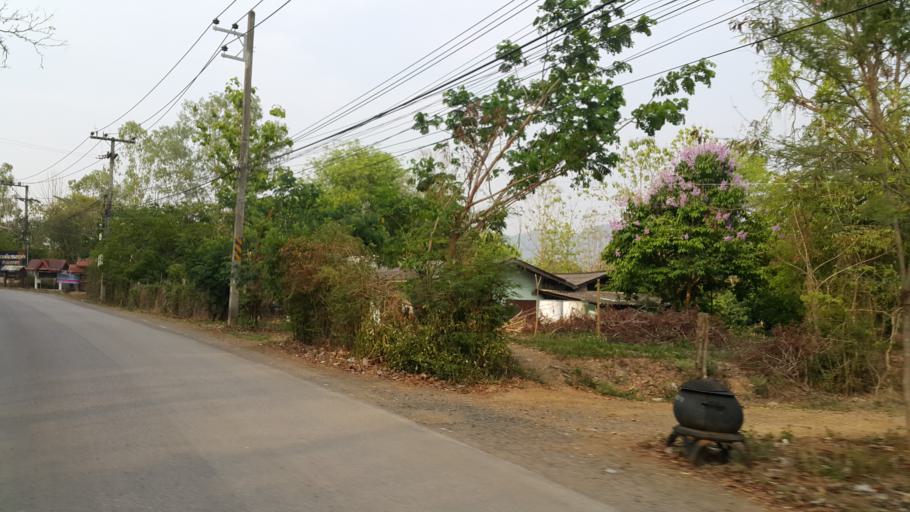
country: TH
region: Chiang Mai
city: Mae On
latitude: 18.7681
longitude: 99.2516
